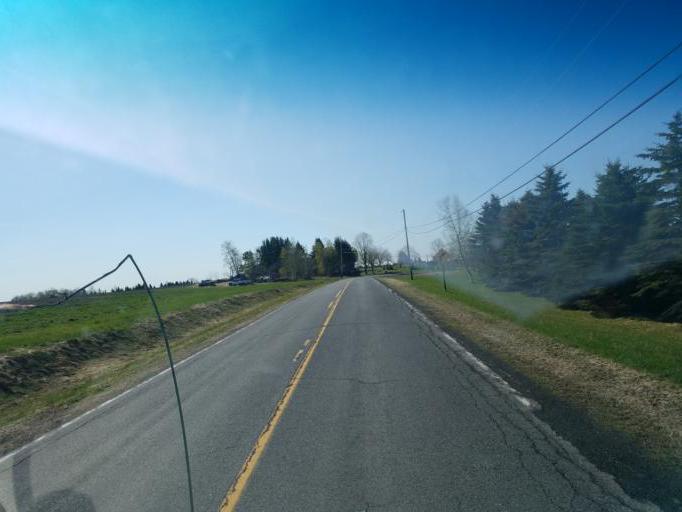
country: US
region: Maine
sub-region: Aroostook County
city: Caribou
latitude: 46.8692
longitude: -68.2102
